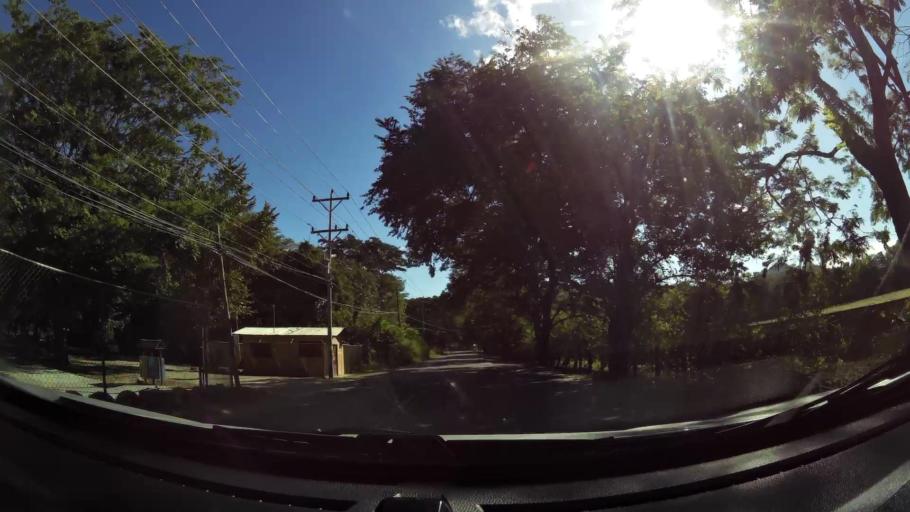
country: CR
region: Guanacaste
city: Sardinal
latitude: 10.4093
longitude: -85.7950
